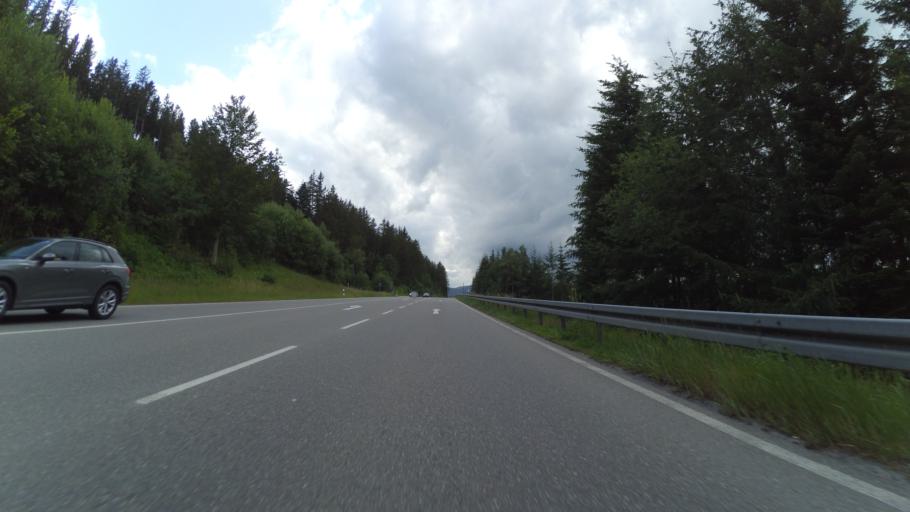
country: DE
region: Baden-Wuerttemberg
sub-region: Freiburg Region
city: Hinterzarten
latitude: 47.8843
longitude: 8.1387
